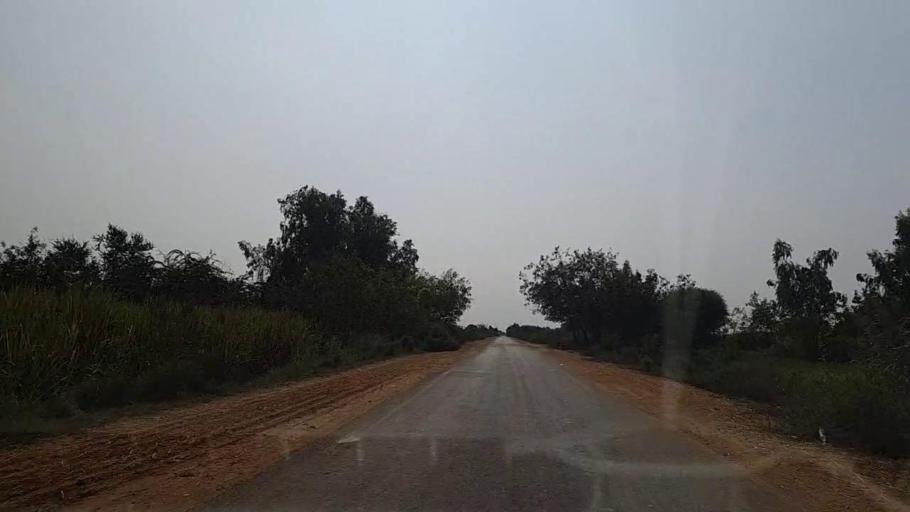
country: PK
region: Sindh
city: Chuhar Jamali
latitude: 24.2618
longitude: 67.9084
